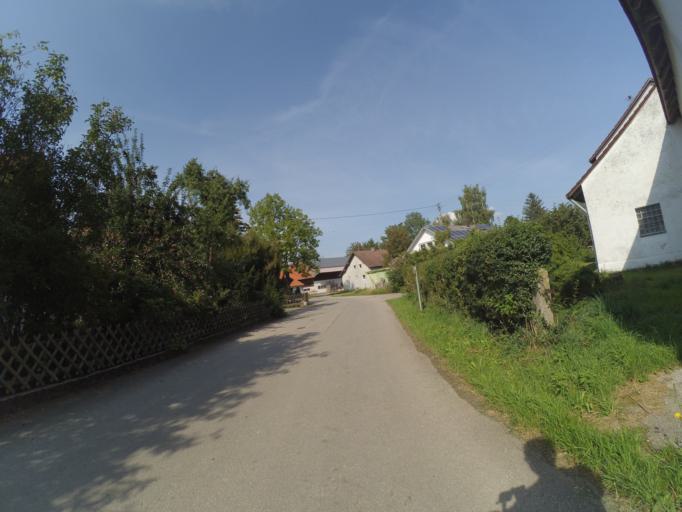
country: DE
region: Bavaria
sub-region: Swabia
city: Lamerdingen
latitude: 48.0824
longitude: 10.7678
